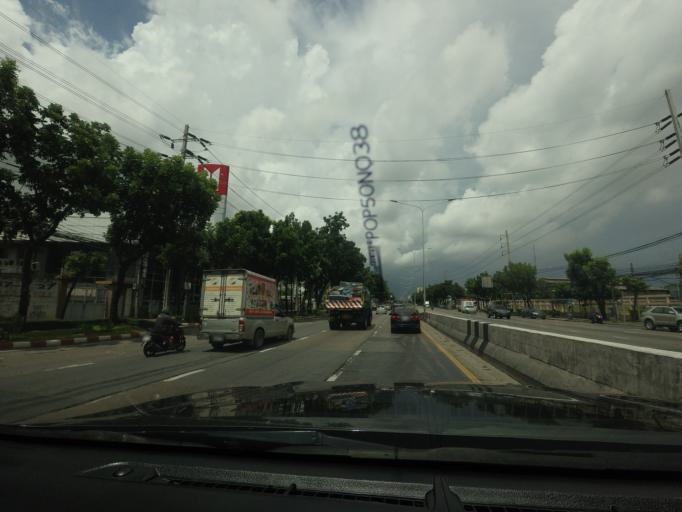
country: TH
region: Bangkok
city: Nong Khaem
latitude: 13.7076
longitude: 100.3732
